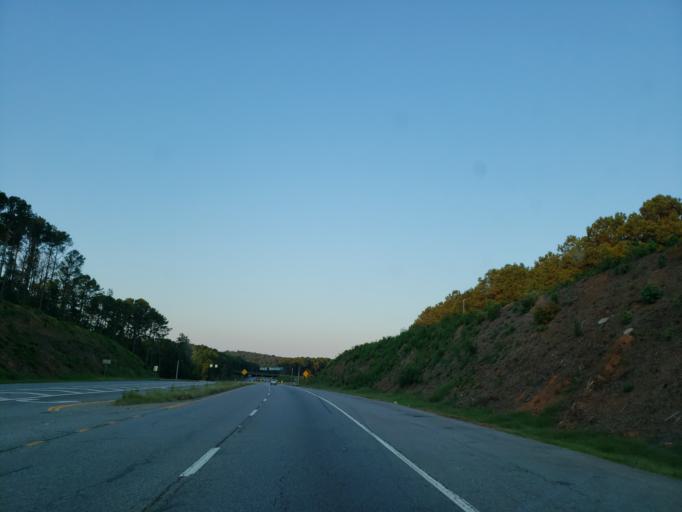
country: US
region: Georgia
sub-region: Bartow County
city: Cartersville
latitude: 34.2180
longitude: -84.8565
